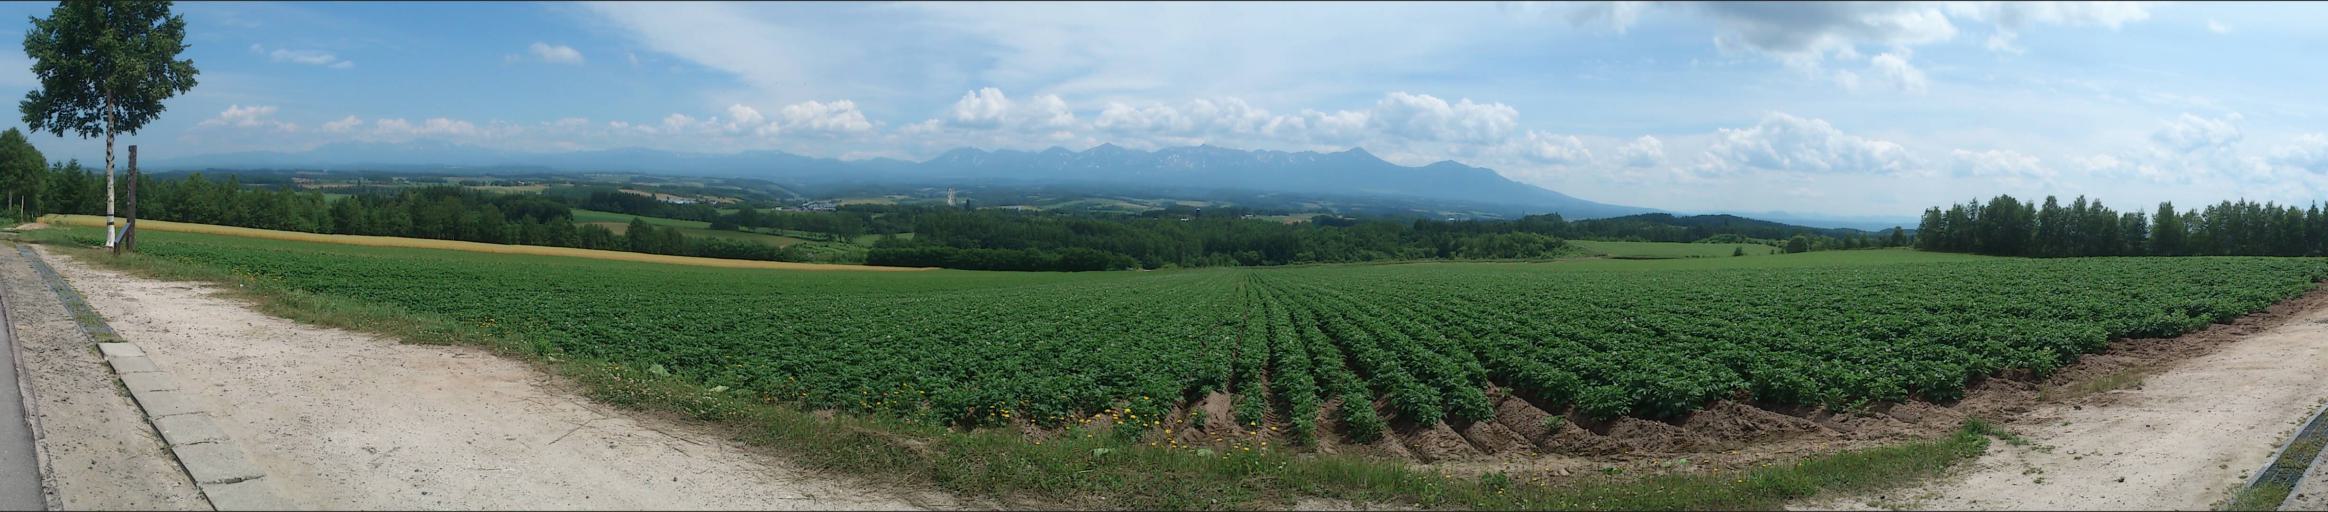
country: JP
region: Hokkaido
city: Shimo-furano
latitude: 43.5210
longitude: 142.4308
